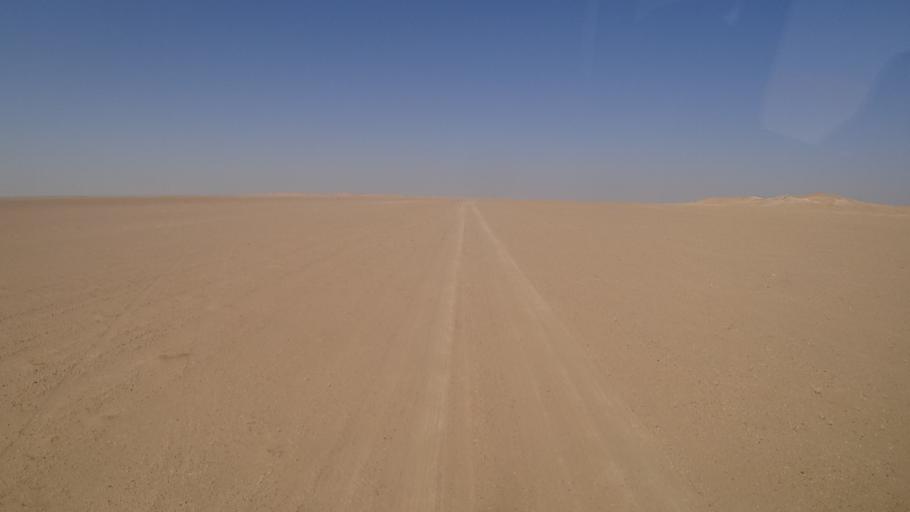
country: YE
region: Al Mahrah
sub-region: Shahan
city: Shihan as Sufla
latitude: 18.5654
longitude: 52.8359
